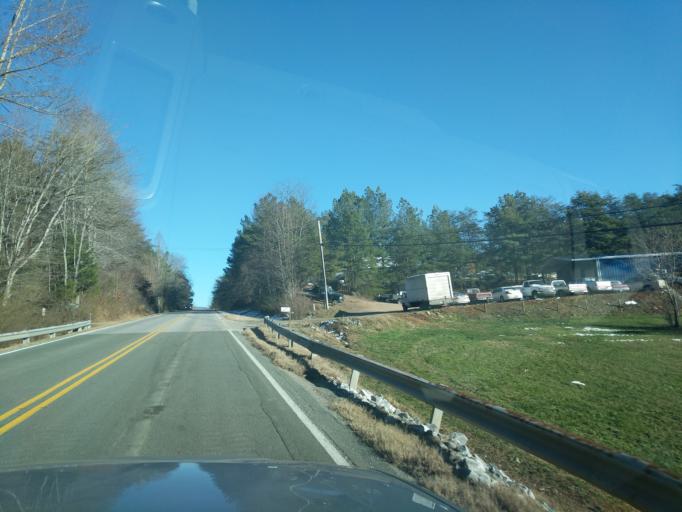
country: US
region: Georgia
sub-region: Towns County
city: Hiawassee
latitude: 34.9251
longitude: -83.6894
